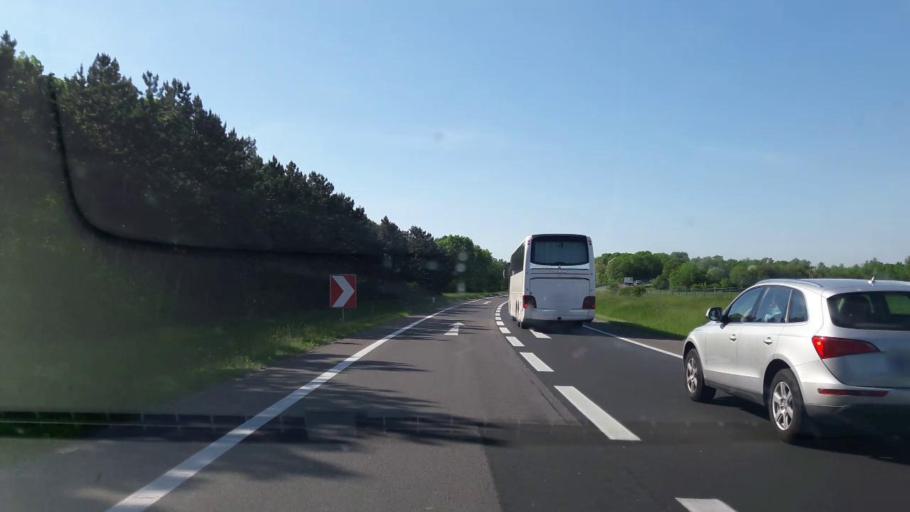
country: AT
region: Burgenland
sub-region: Eisenstadt-Umgebung
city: Wulkaprodersdorf
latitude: 47.8177
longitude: 16.4923
